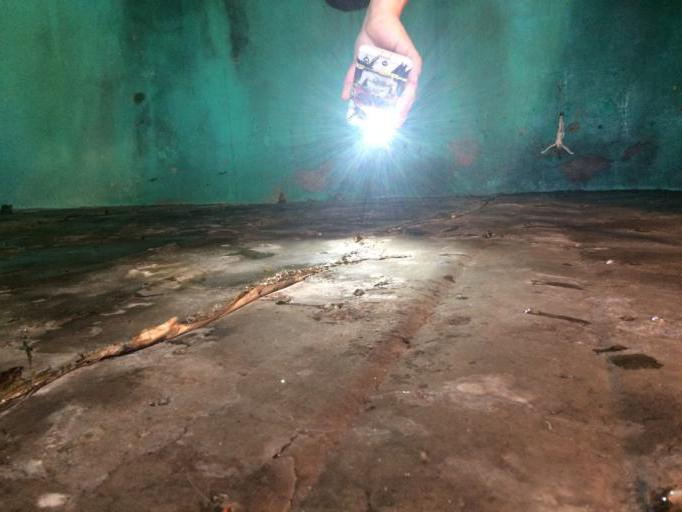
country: MX
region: Mexico
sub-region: Ocuilan
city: Plaza Nueva
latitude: 18.9149
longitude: -99.4546
